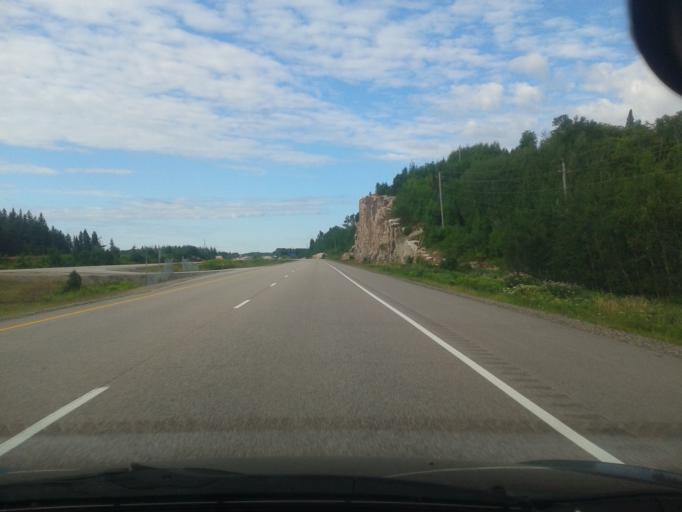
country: CA
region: Ontario
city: Powassan
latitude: 46.0181
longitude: -79.3454
